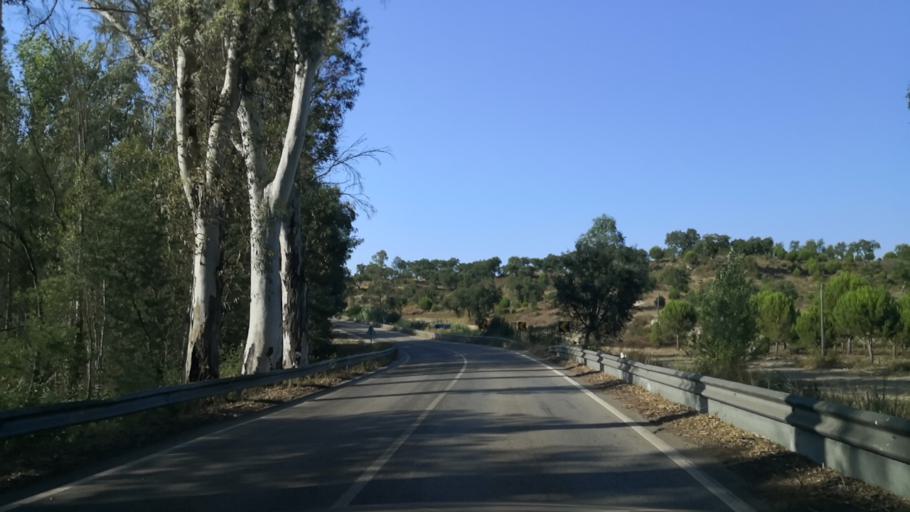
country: PT
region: Santarem
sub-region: Almeirim
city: Fazendas de Almeirim
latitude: 39.0652
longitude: -8.5648
